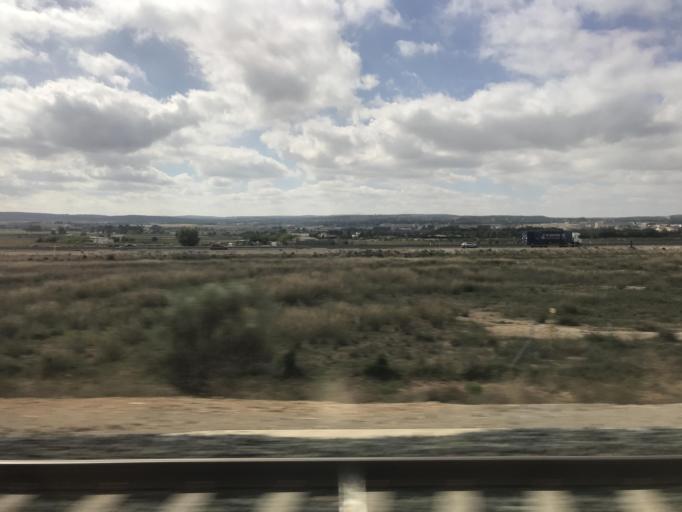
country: ES
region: Castille-La Mancha
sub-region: Provincia de Albacete
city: Almansa
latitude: 38.8782
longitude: -1.0680
